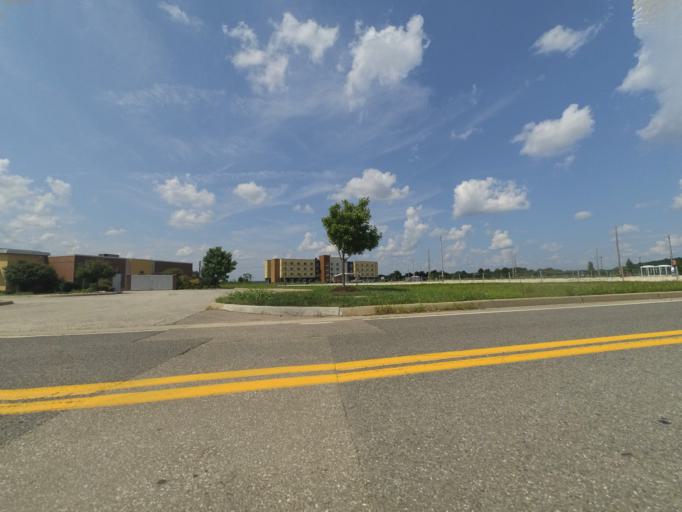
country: US
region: West Virginia
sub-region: Cabell County
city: Huntington
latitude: 38.3939
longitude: -82.4220
